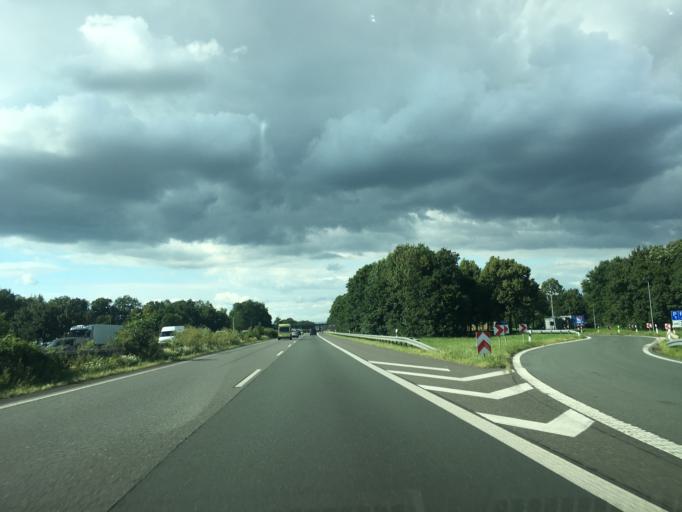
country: DE
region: North Rhine-Westphalia
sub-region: Regierungsbezirk Munster
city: Ascheberg
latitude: 51.7717
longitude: 7.6404
